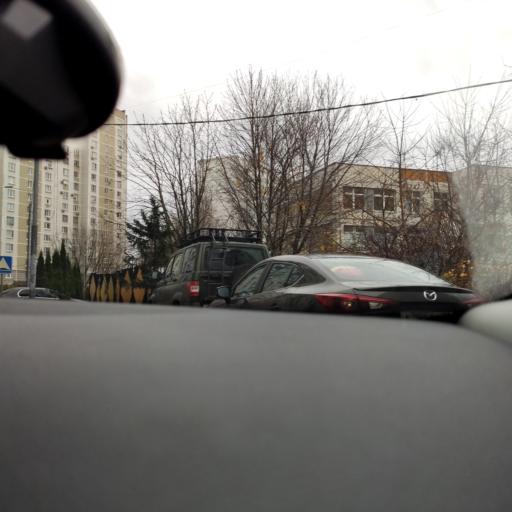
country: RU
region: Moskovskaya
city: Pavshino
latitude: 55.8432
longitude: 37.3661
